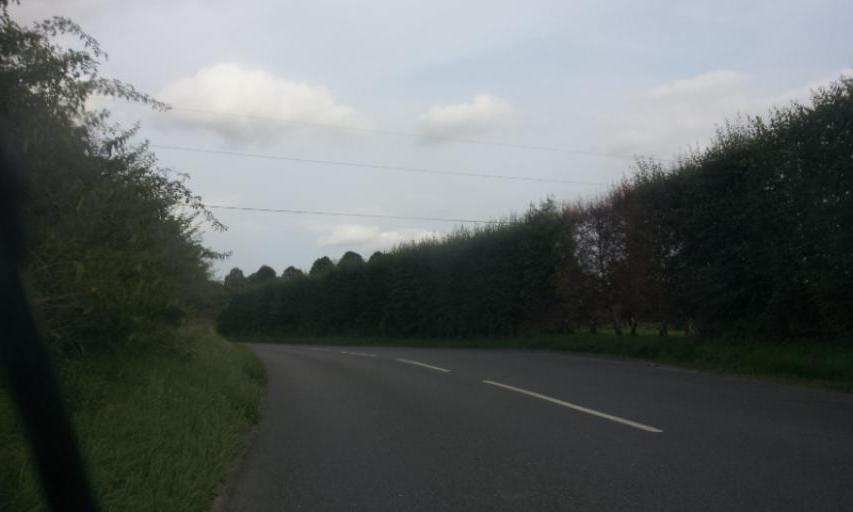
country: GB
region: England
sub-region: Kent
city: Hadlow
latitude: 51.2120
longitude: 0.3275
